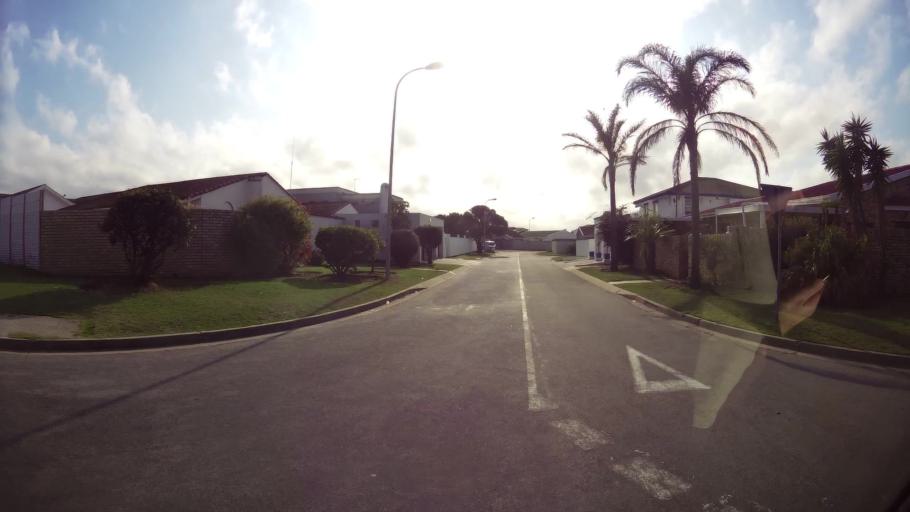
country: ZA
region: Eastern Cape
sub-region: Nelson Mandela Bay Metropolitan Municipality
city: Port Elizabeth
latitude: -33.9231
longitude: 25.5609
